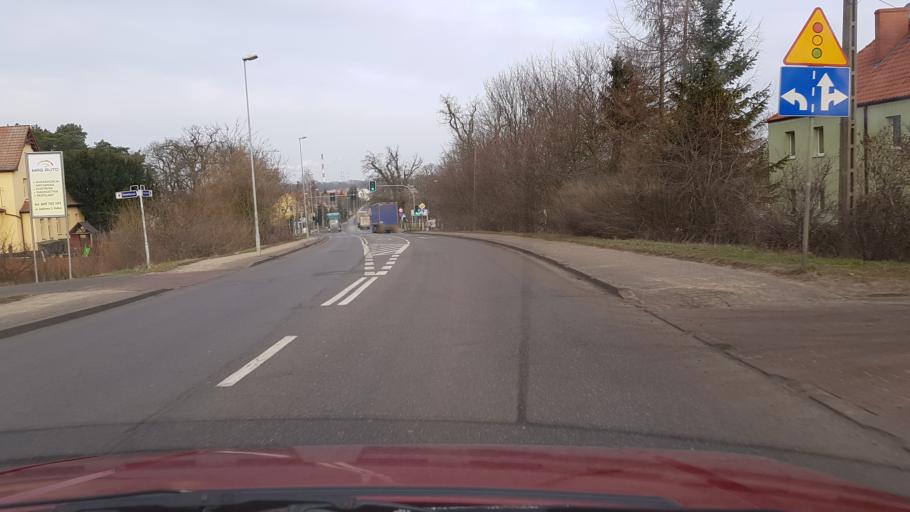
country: PL
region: West Pomeranian Voivodeship
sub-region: Powiat policki
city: Police
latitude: 53.5384
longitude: 14.5781
